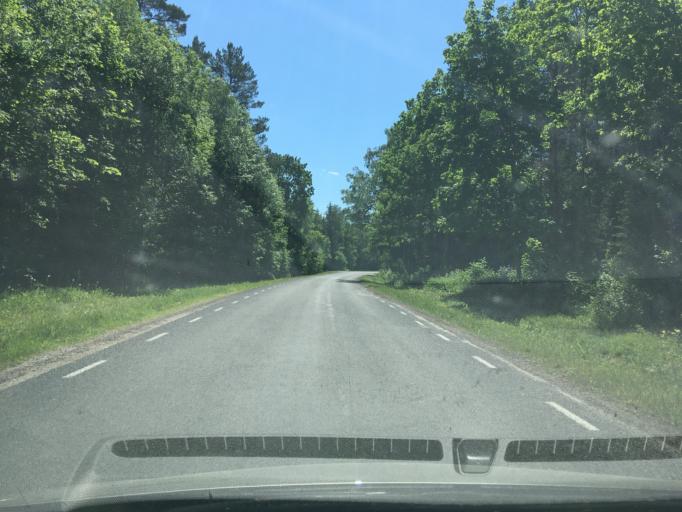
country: EE
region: Raplamaa
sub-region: Kohila vald
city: Kohila
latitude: 59.1575
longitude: 24.8519
